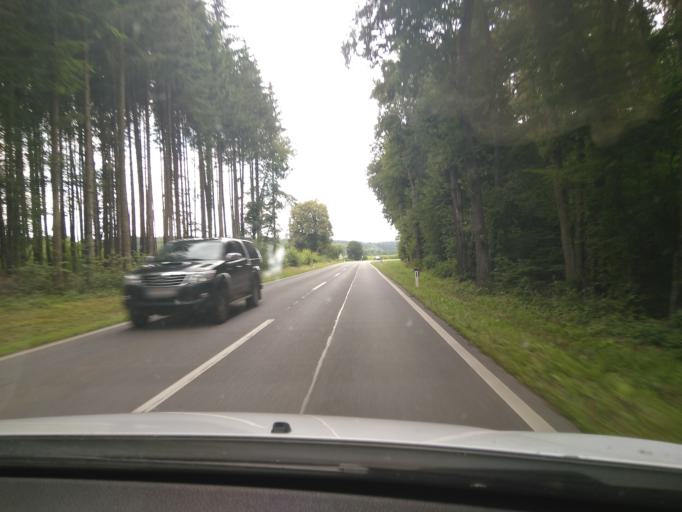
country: AT
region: Burgenland
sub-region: Politischer Bezirk Oberwart
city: Oberschutzen
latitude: 47.3502
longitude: 16.1742
